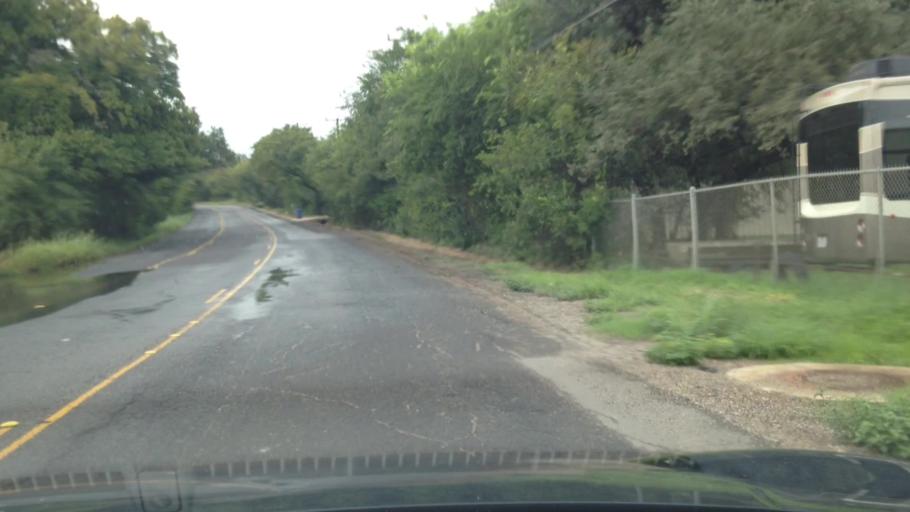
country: US
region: Texas
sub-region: Bexar County
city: Hollywood Park
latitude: 29.5865
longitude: -98.4236
